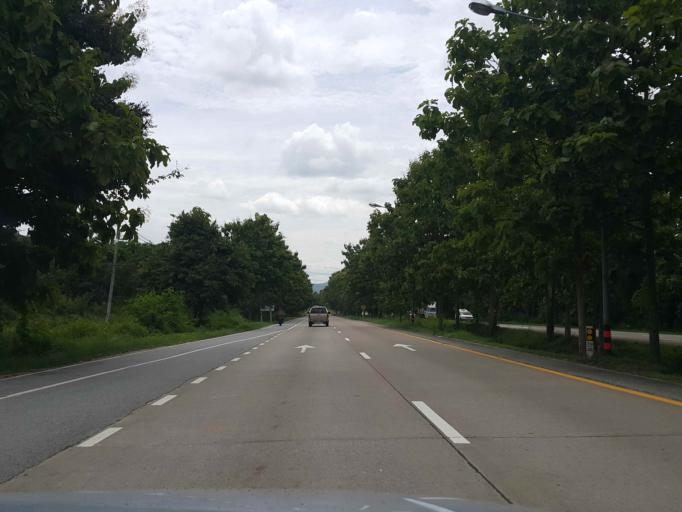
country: TH
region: Lamphun
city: Mae Tha
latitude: 18.4864
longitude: 99.1305
